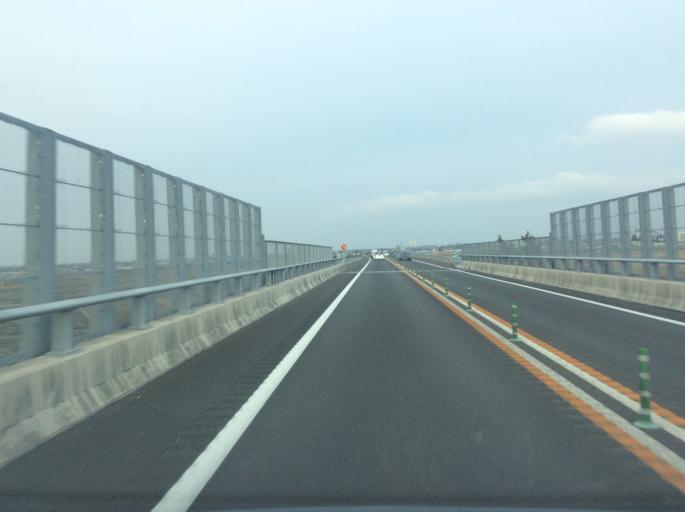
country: JP
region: Miyagi
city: Watari
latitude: 38.0144
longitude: 140.8850
